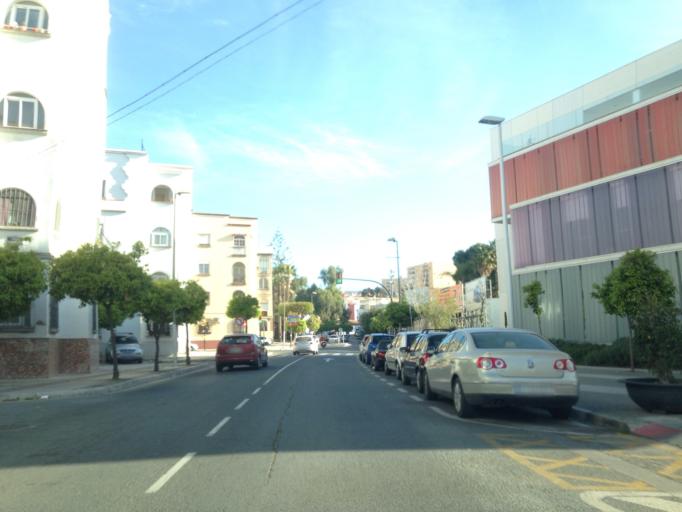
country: ES
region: Andalusia
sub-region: Provincia de Malaga
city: Malaga
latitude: 36.7321
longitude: -4.4243
